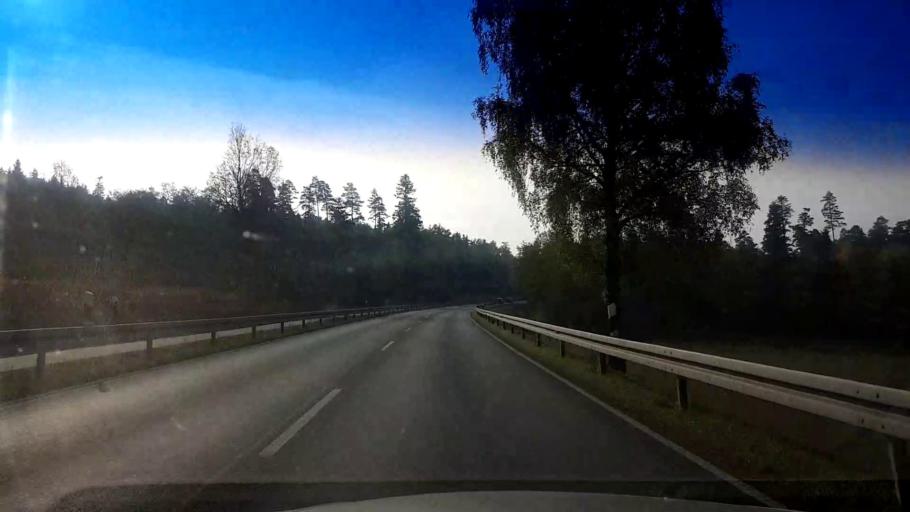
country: DE
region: Bavaria
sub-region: Upper Franconia
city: Neuenmarkt
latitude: 50.0886
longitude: 11.6100
